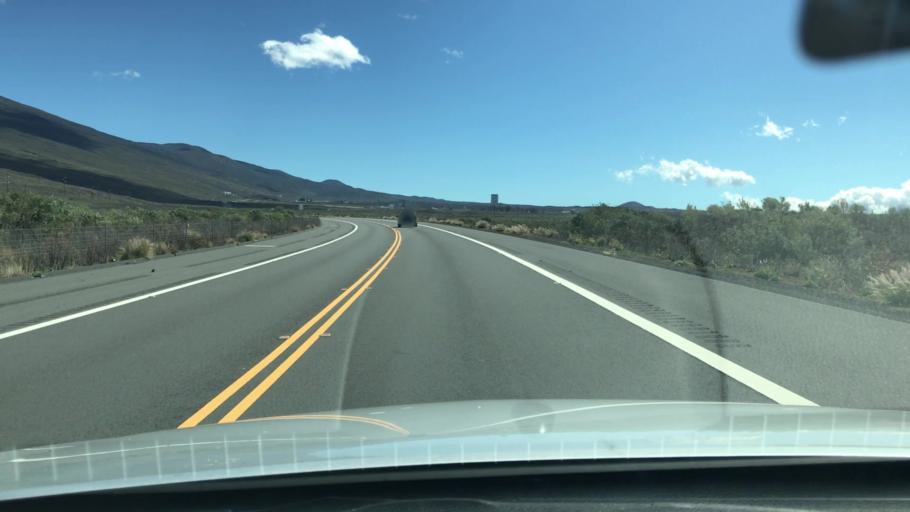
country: US
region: Hawaii
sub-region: Hawaii County
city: Waikoloa
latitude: 19.7676
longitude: -155.5825
